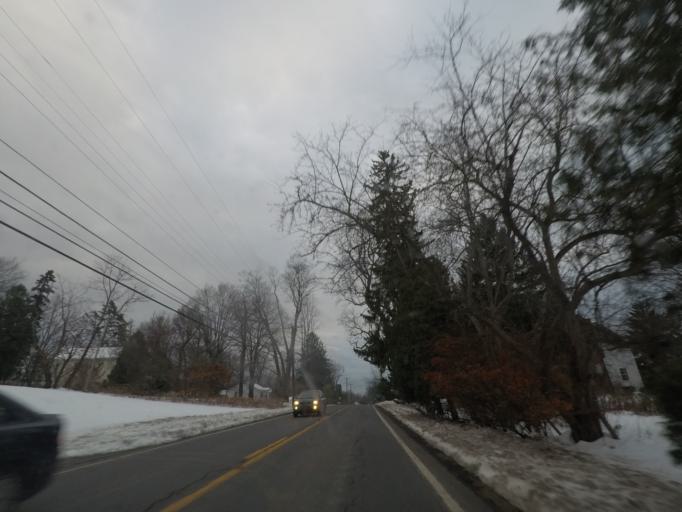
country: US
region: New York
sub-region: Ulster County
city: Clintondale
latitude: 41.6699
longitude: -74.1053
